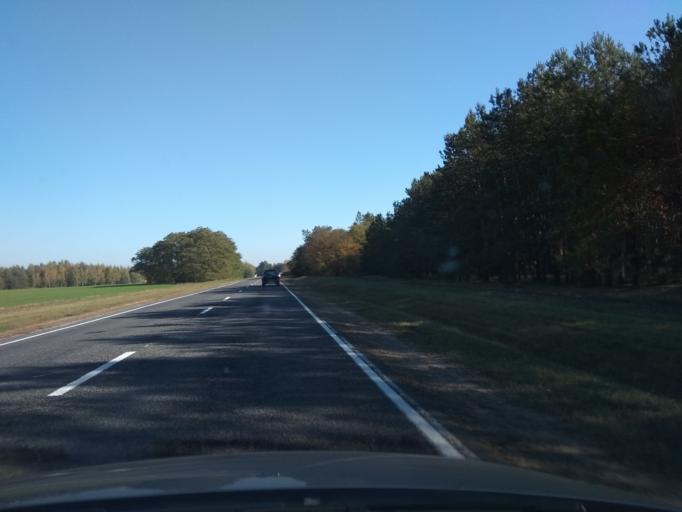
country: BY
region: Brest
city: Kobryn
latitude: 52.1140
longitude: 24.2974
